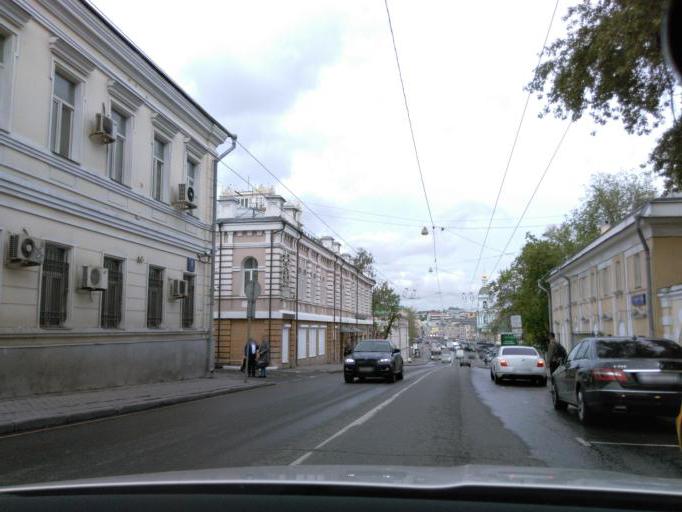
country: RU
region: Moscow
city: Zamoskvorech'ye
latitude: 55.7468
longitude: 37.6475
